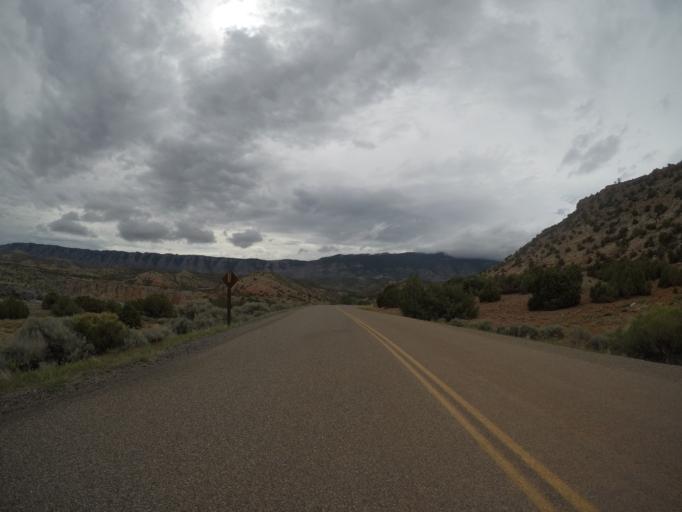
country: US
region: Wyoming
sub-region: Big Horn County
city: Lovell
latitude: 45.0963
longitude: -108.2112
